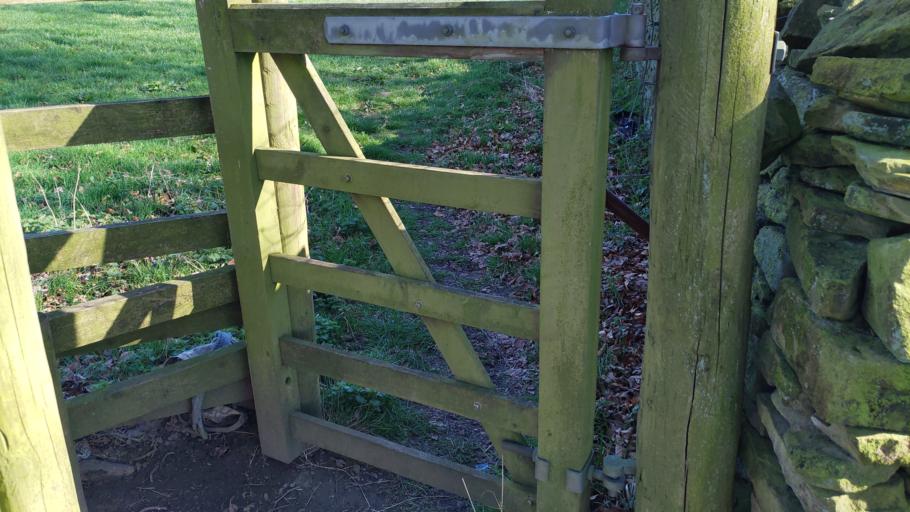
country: GB
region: England
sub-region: Borough of Bolton
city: Horwich
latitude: 53.6297
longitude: -2.5578
